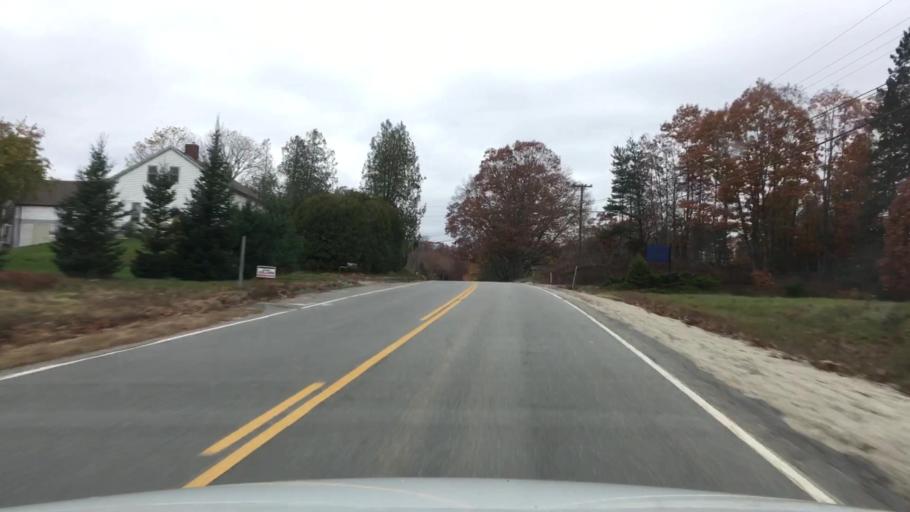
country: US
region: Maine
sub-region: Hancock County
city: Sedgwick
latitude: 44.3911
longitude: -68.5808
